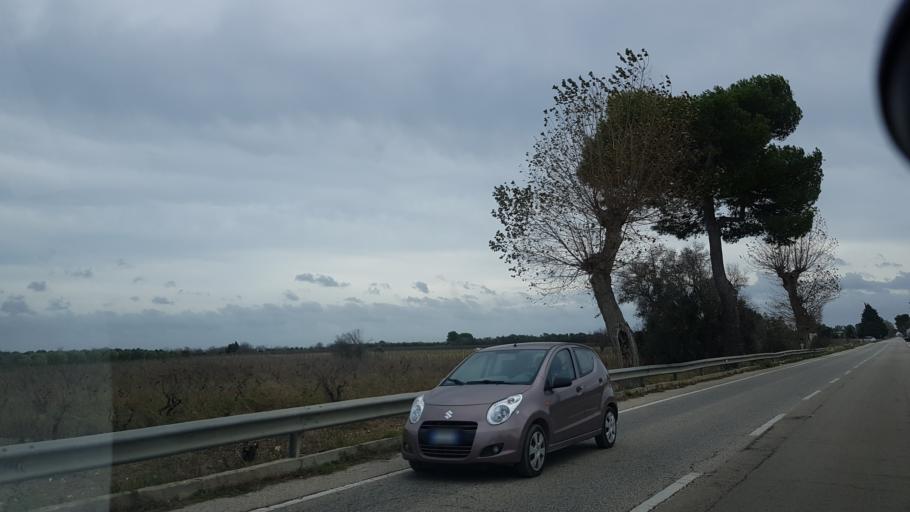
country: IT
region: Apulia
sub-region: Provincia di Brindisi
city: San Pancrazio Salentino
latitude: 40.4143
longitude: 17.8550
